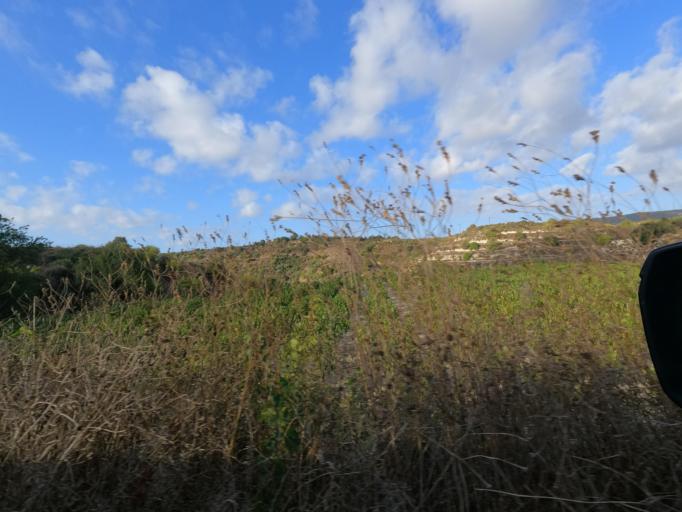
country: CY
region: Pafos
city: Mesogi
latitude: 34.8323
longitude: 32.5271
